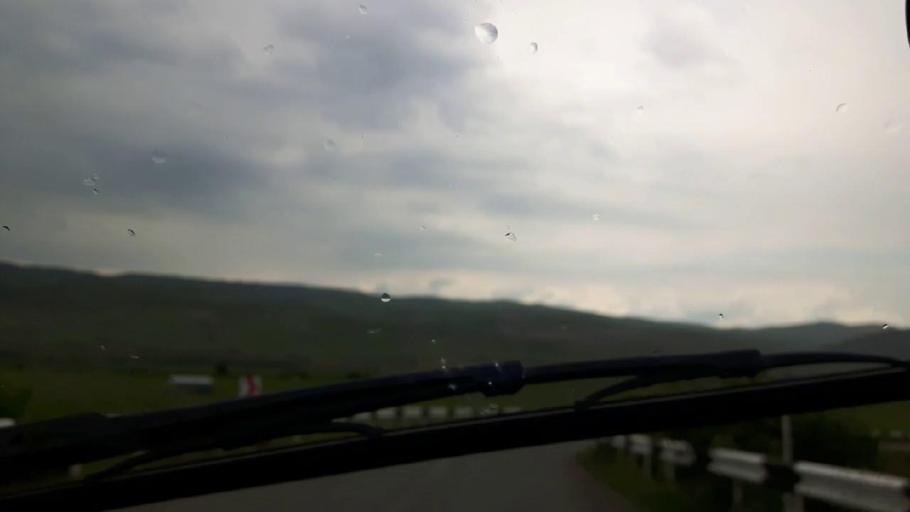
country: GE
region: Shida Kartli
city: Gori
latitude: 41.9632
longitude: 44.1891
